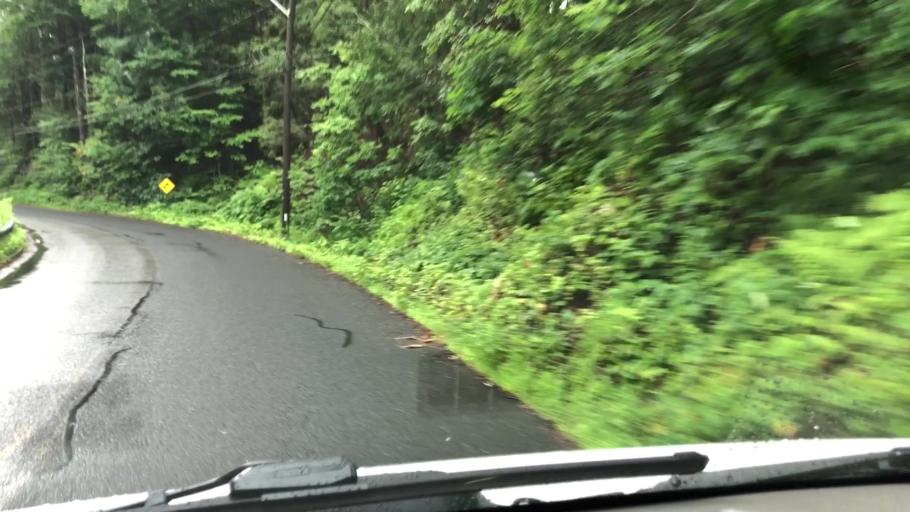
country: US
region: Massachusetts
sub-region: Hampshire County
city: Williamsburg
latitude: 42.3615
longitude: -72.7028
